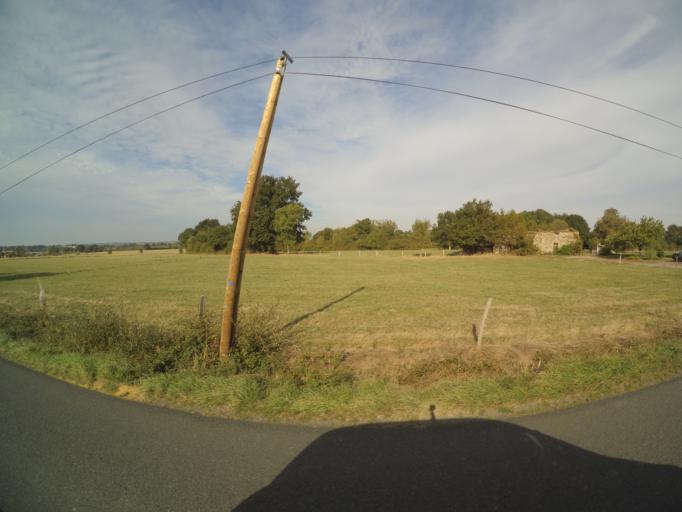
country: FR
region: Pays de la Loire
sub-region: Departement de Maine-et-Loire
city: Geste
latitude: 47.1698
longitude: -1.1285
